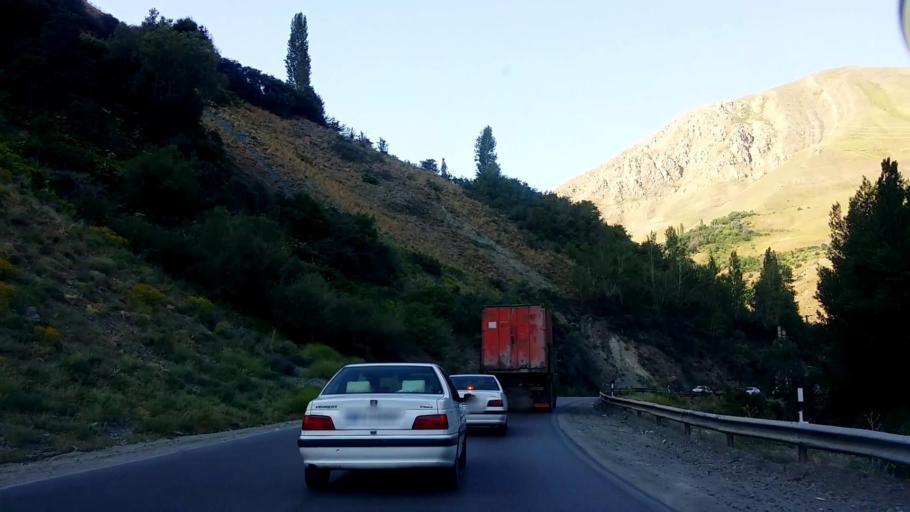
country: IR
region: Tehran
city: Tajrish
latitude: 36.1045
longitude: 51.3174
